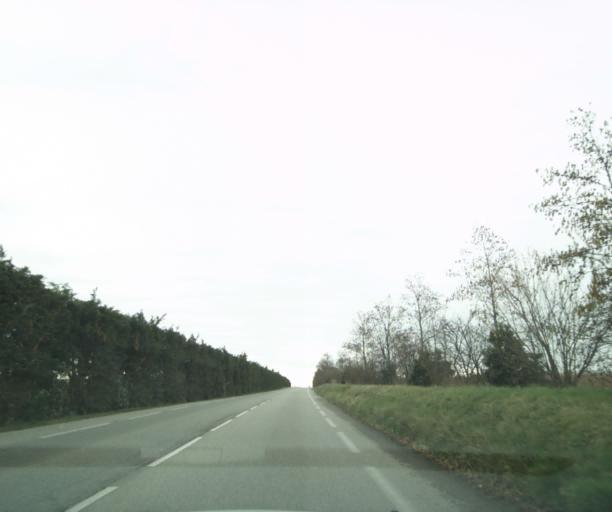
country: FR
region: Rhone-Alpes
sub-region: Departement de la Drome
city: Bourg-les-Valence
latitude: 44.9764
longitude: 4.9038
